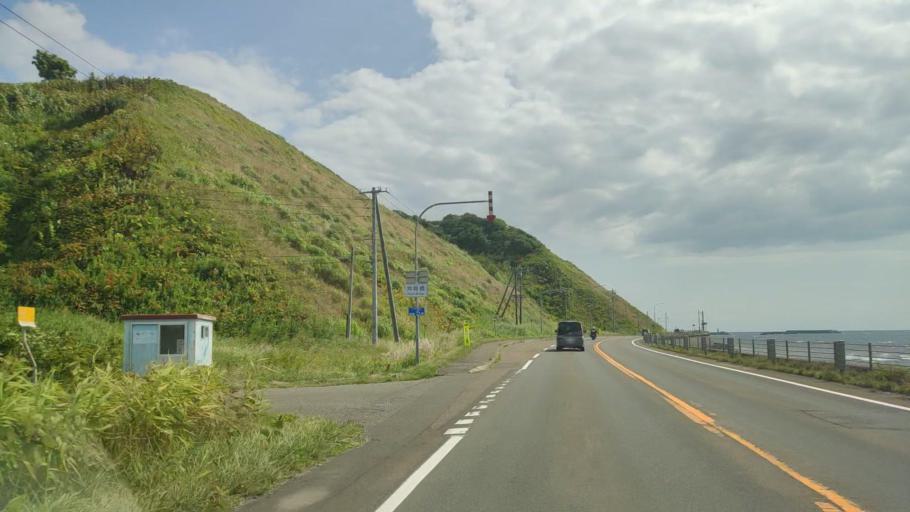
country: JP
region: Hokkaido
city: Rumoi
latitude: 44.2360
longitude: 141.6570
